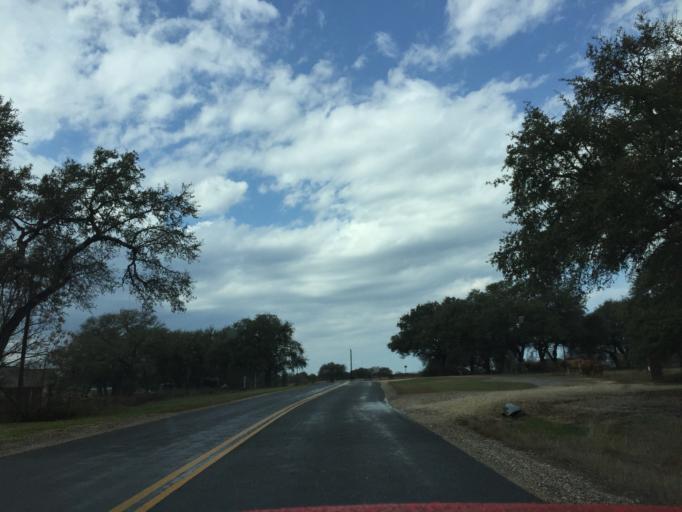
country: US
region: Texas
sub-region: Burnet County
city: Bertram
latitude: 30.6268
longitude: -97.9832
